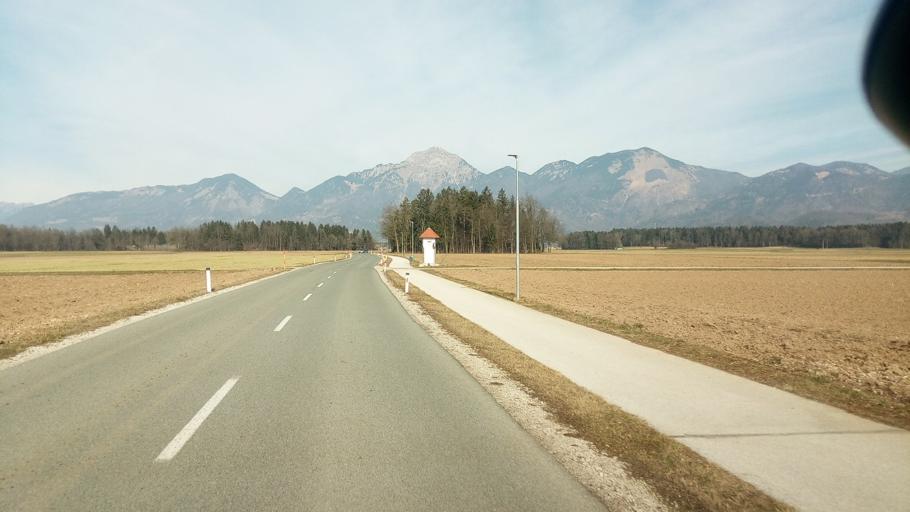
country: SI
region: Sencur
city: Sencur
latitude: 46.2550
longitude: 14.4191
